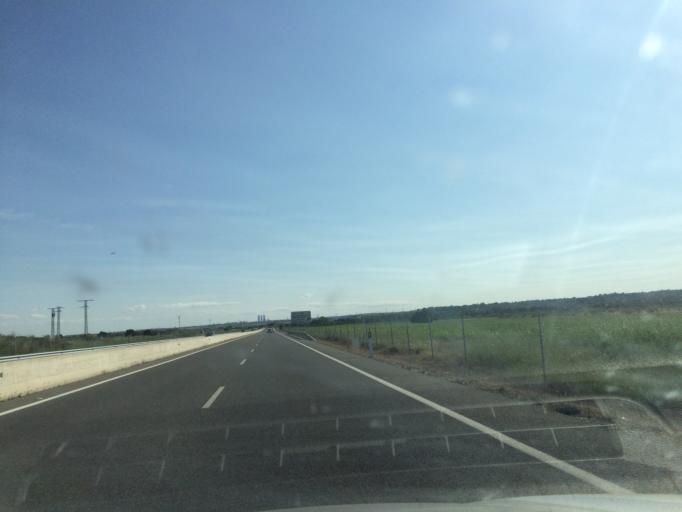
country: ES
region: Madrid
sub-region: Provincia de Madrid
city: Fuente el Saz
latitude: 40.6047
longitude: -3.5516
